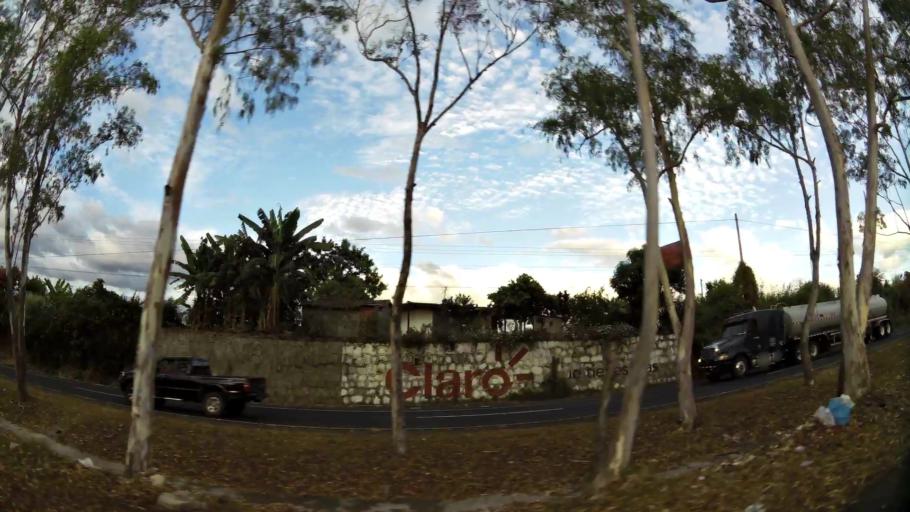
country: SV
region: San Vicente
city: San Vicente
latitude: 13.6742
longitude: -88.8440
